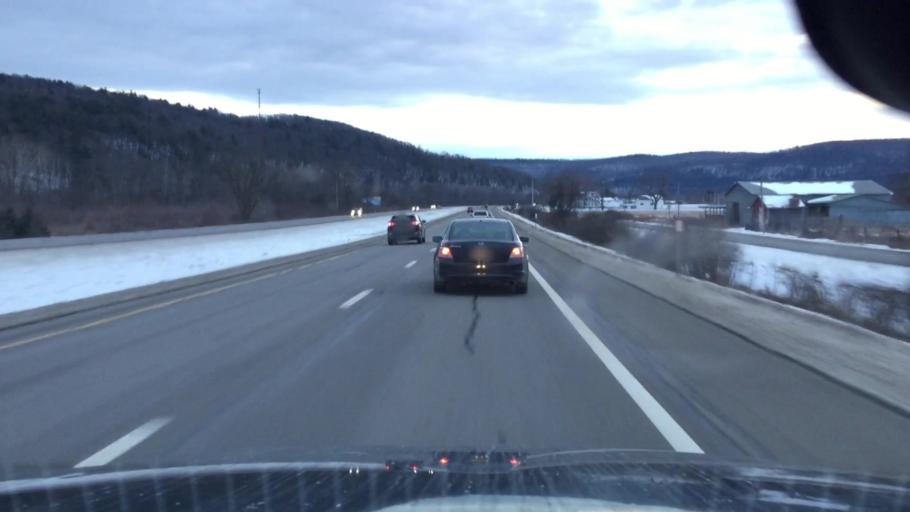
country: US
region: New York
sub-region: Steuben County
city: Gang Mills
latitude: 42.2045
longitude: -77.1677
